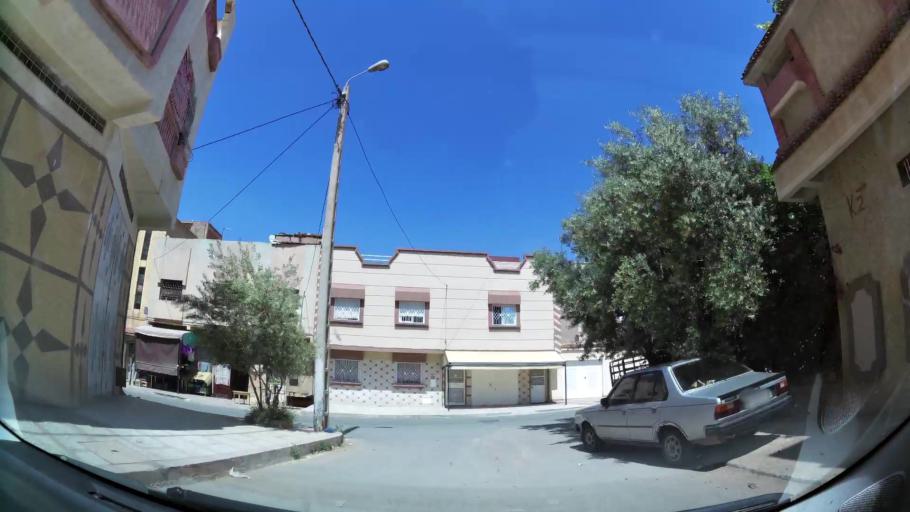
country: MA
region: Oriental
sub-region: Oujda-Angad
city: Oujda
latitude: 34.6934
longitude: -1.8827
